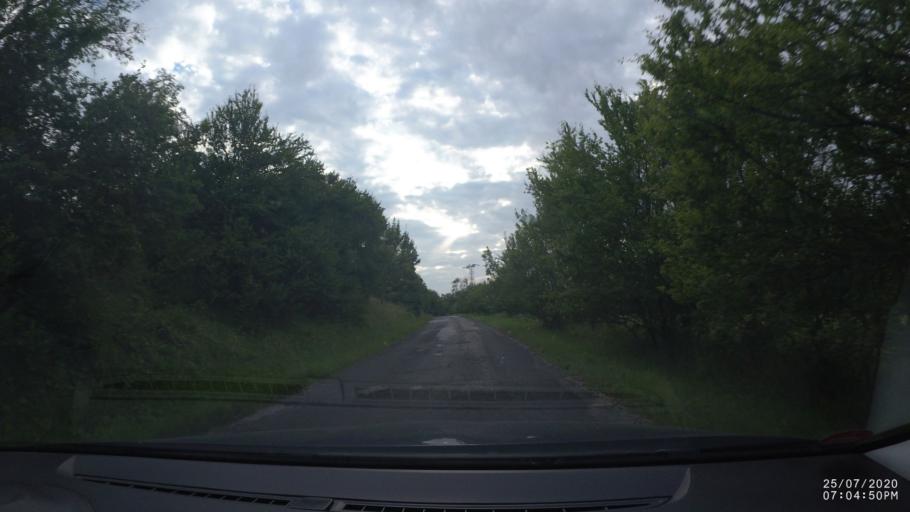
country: CZ
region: Kralovehradecky
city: Horice
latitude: 50.3665
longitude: 15.6524
